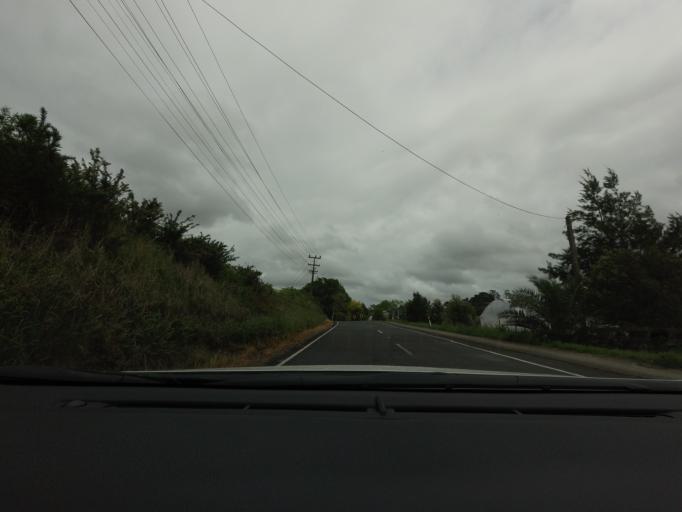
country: NZ
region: Auckland
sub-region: Auckland
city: Waitakere
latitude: -36.8958
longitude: 174.6020
